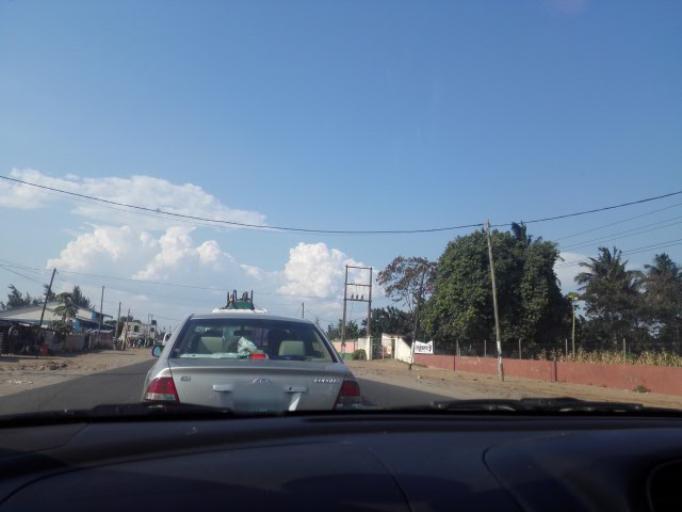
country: MZ
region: Maputo City
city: Maputo
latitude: -25.8580
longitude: 32.5670
